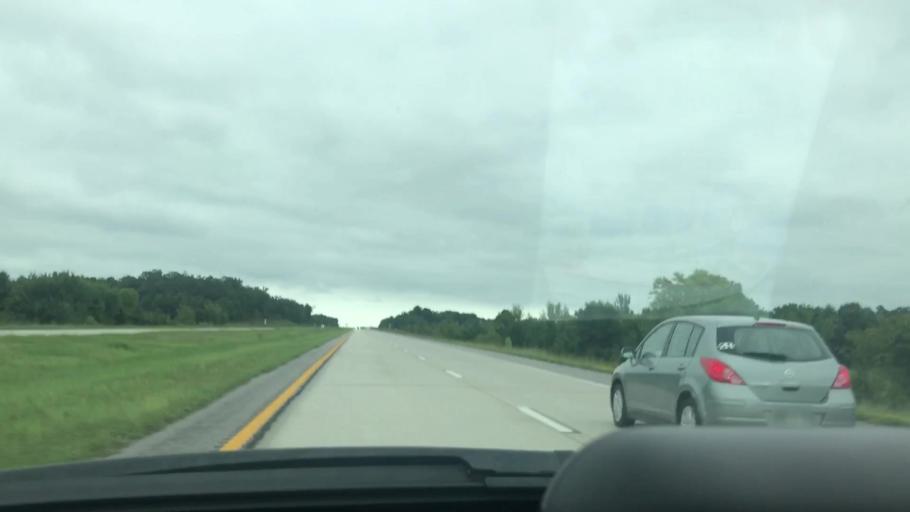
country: US
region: Missouri
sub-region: Greene County
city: Fair Grove
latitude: 37.4688
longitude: -93.1395
